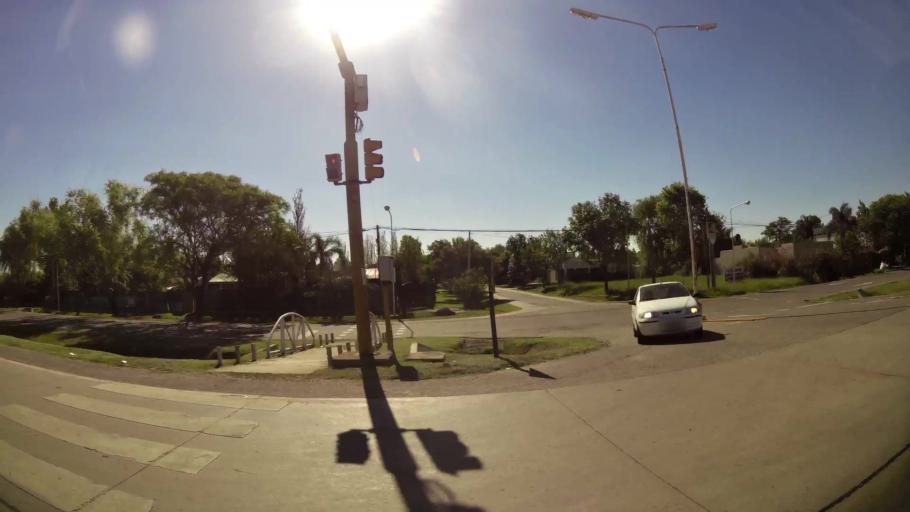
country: AR
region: Santa Fe
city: Rafaela
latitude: -31.2854
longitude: -61.5136
